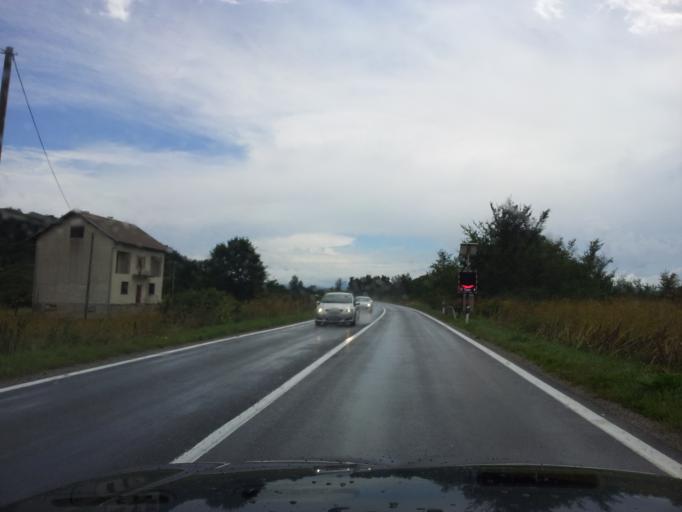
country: BA
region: Federation of Bosnia and Herzegovina
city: Bihac
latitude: 44.6426
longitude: 15.7207
